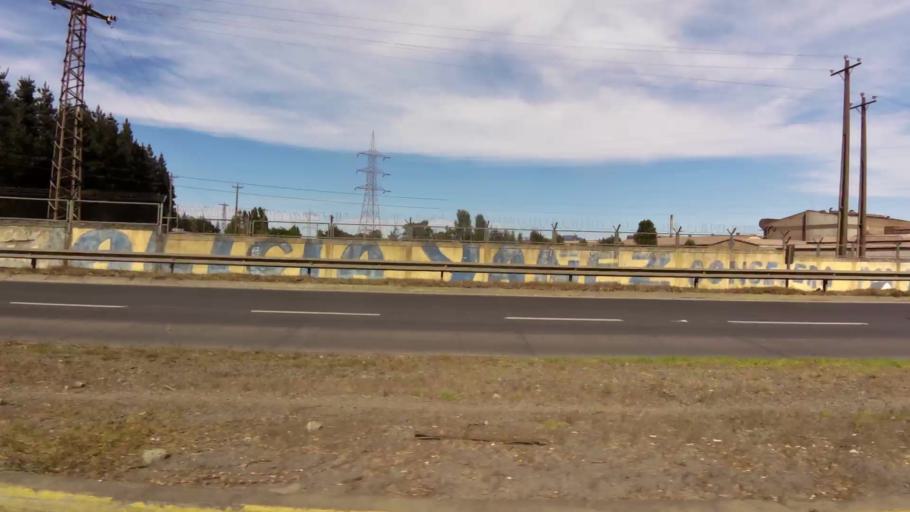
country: CL
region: Biobio
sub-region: Provincia de Concepcion
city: Talcahuano
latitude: -36.7496
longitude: -73.1244
